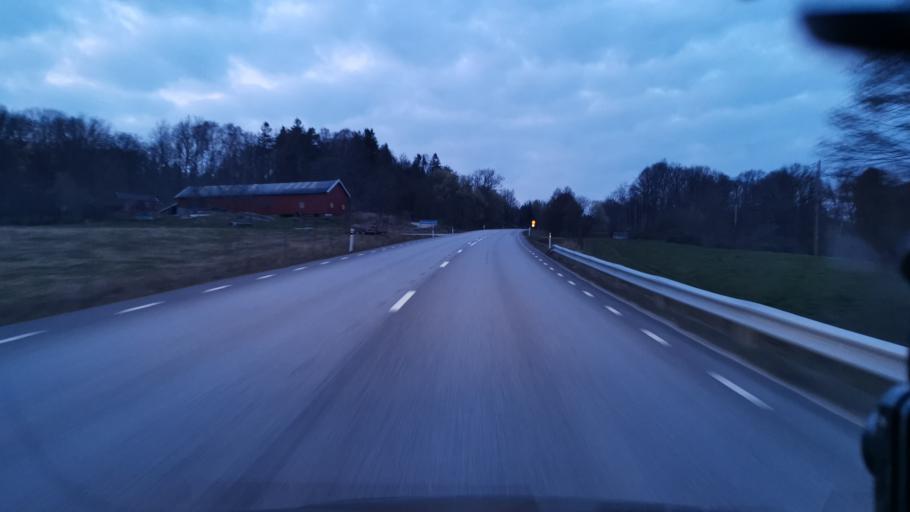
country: SE
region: Vaestra Goetaland
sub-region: Orust
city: Henan
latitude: 58.2795
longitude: 11.6943
